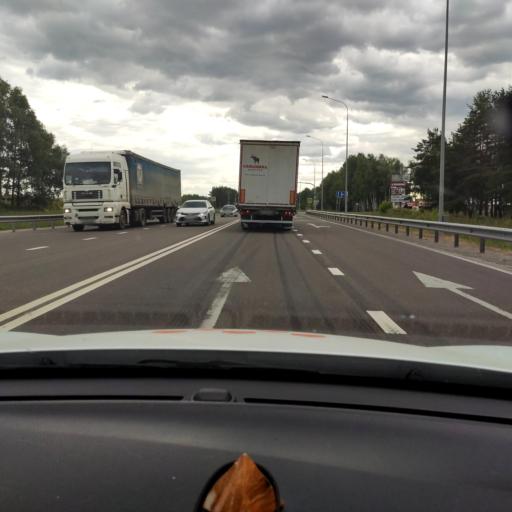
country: RU
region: Mariy-El
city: Pomary
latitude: 55.9214
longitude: 48.3732
